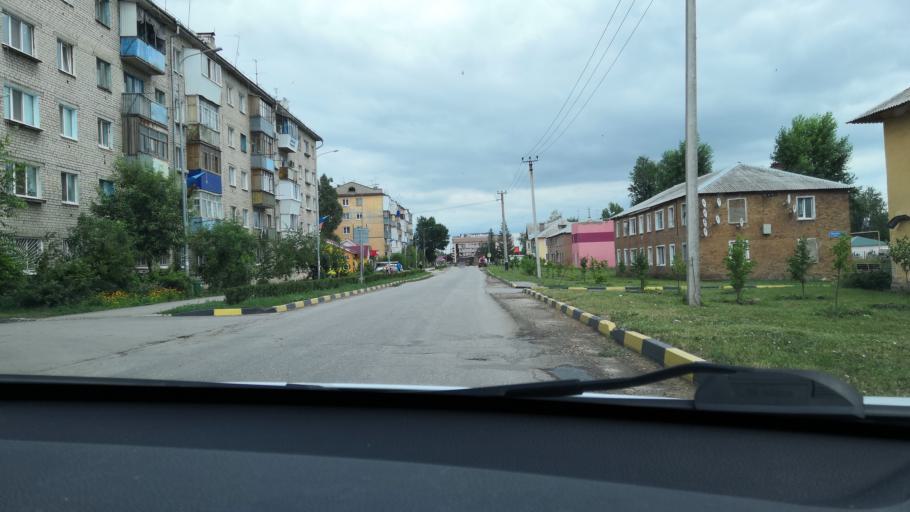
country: RU
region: Samara
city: Smyshlyayevka
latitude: 53.2696
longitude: 50.3906
